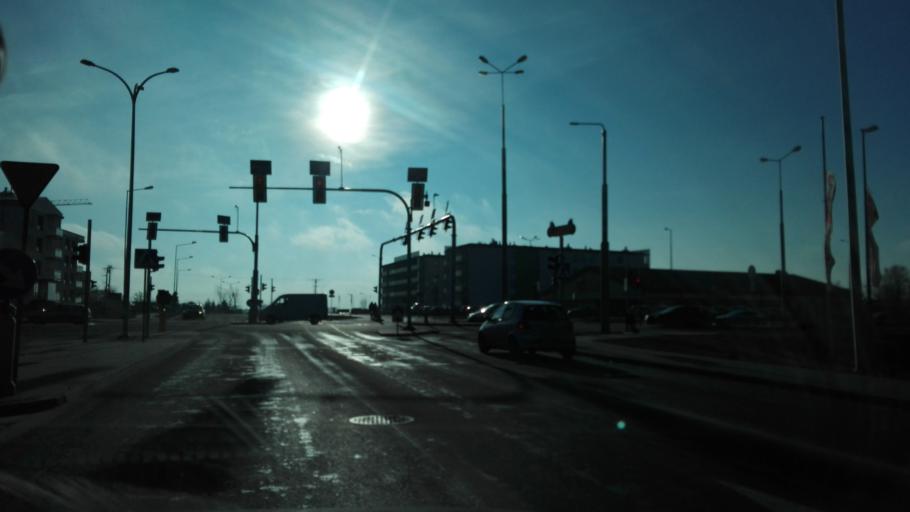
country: PL
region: Lublin Voivodeship
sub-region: Powiat lubelski
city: Kozubszczyzna
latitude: 51.2272
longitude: 22.4800
